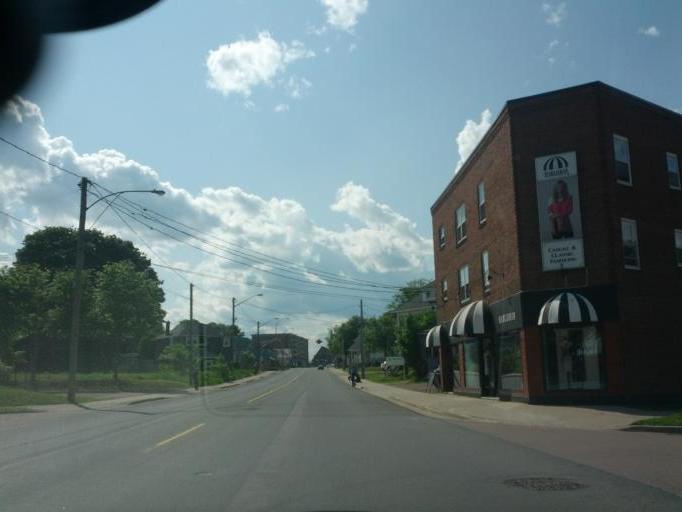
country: CA
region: New Brunswick
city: Moncton
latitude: 46.0956
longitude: -64.7886
